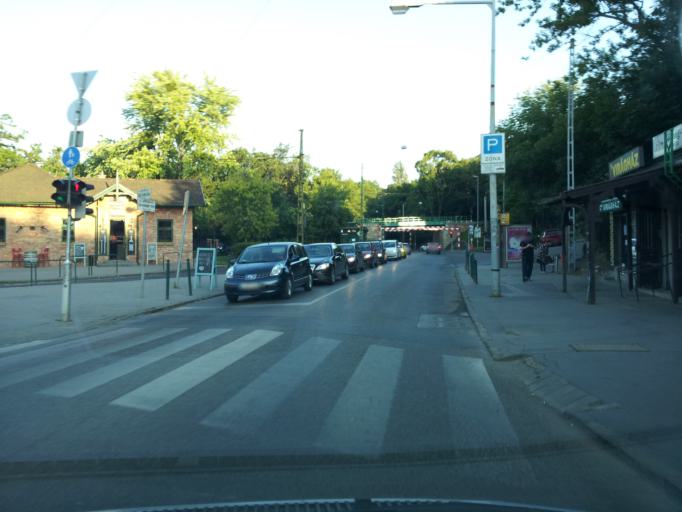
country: HU
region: Budapest
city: Budapest XII. keruelet
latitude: 47.5100
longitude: 19.0087
